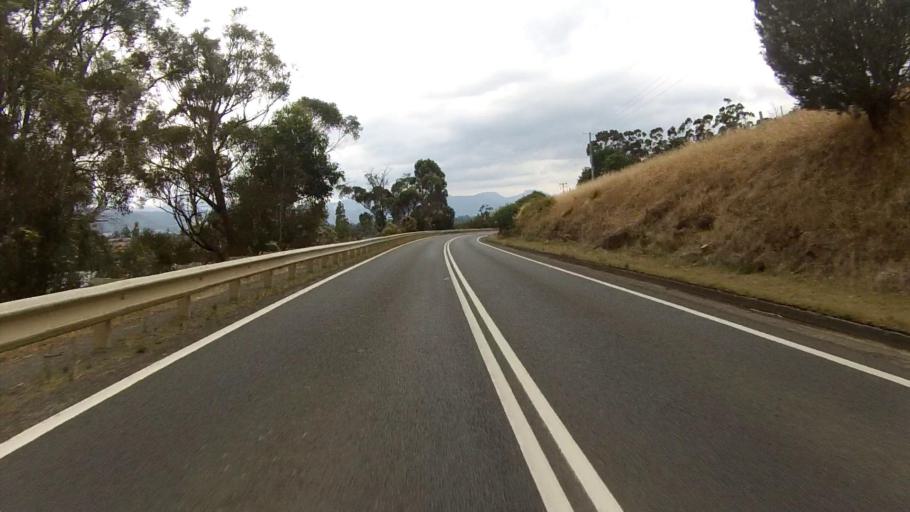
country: AU
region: Tasmania
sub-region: Huon Valley
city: Huonville
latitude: -43.0450
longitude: 147.0511
